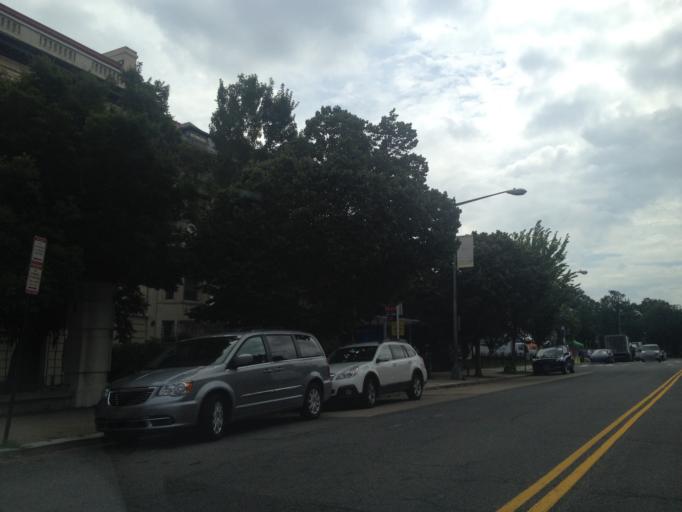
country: US
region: Washington, D.C.
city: Washington, D.C.
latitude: 38.9104
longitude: -77.0458
